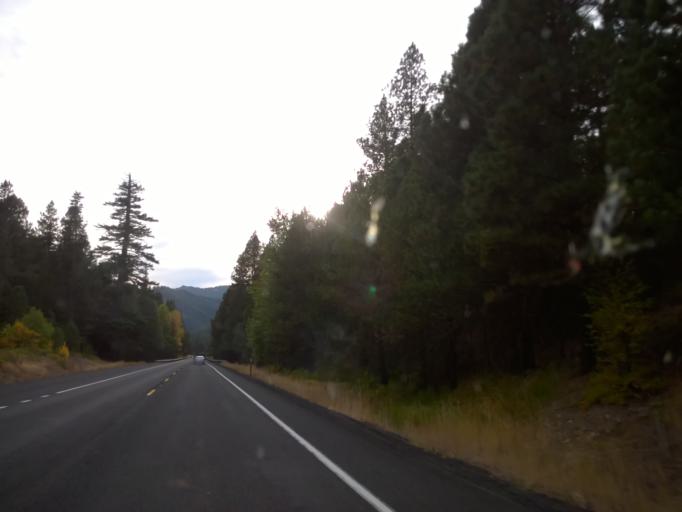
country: US
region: Washington
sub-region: Chelan County
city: Leavenworth
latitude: 47.3281
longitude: -120.6628
